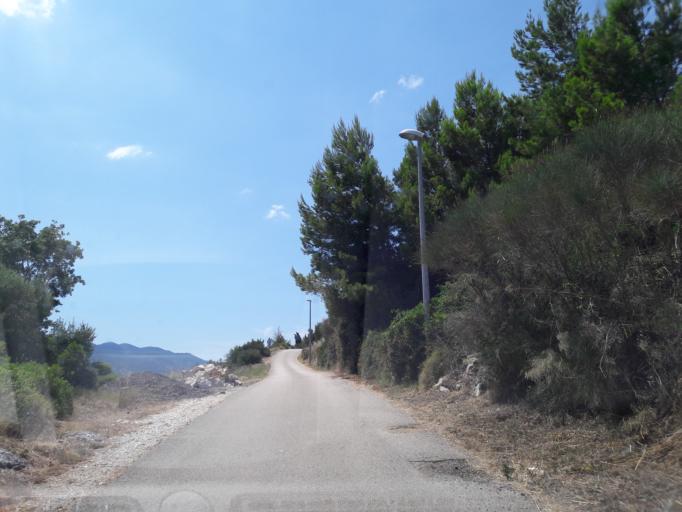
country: HR
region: Dubrovacko-Neretvanska
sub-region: Grad Korcula
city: Zrnovo
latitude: 42.9839
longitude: 17.0822
